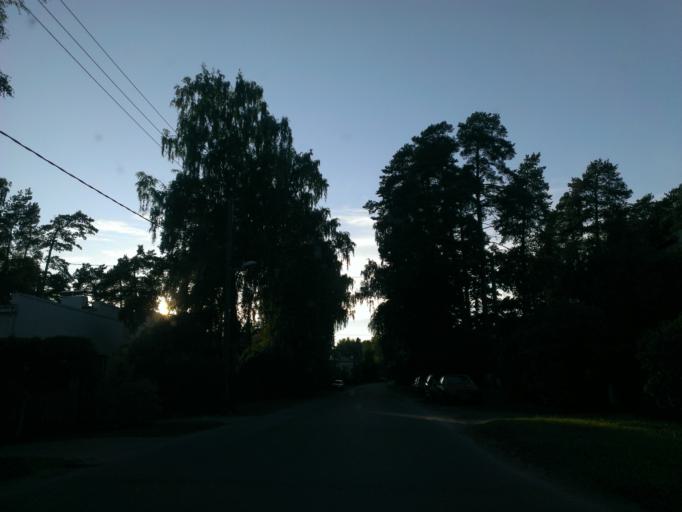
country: LV
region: Riga
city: Bergi
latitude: 56.9801
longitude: 24.3044
